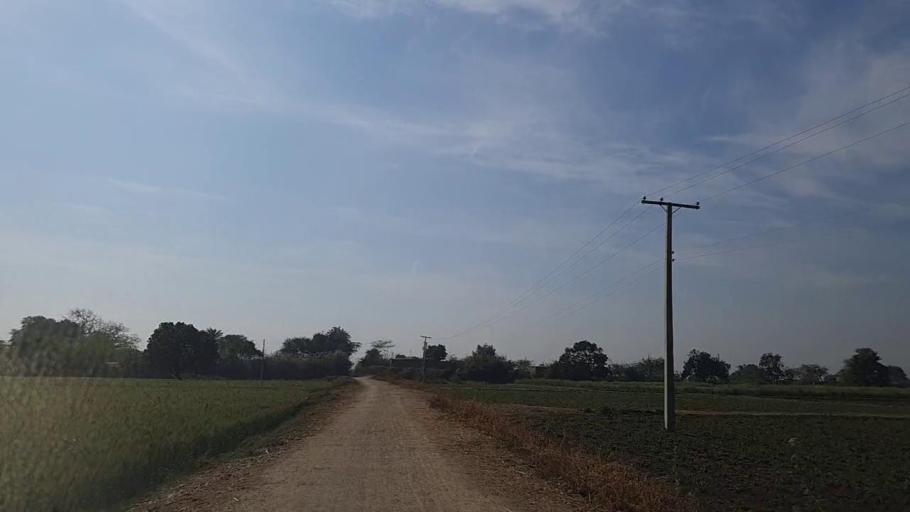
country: PK
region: Sindh
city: Mirpur Khas
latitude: 25.4707
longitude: 68.9745
